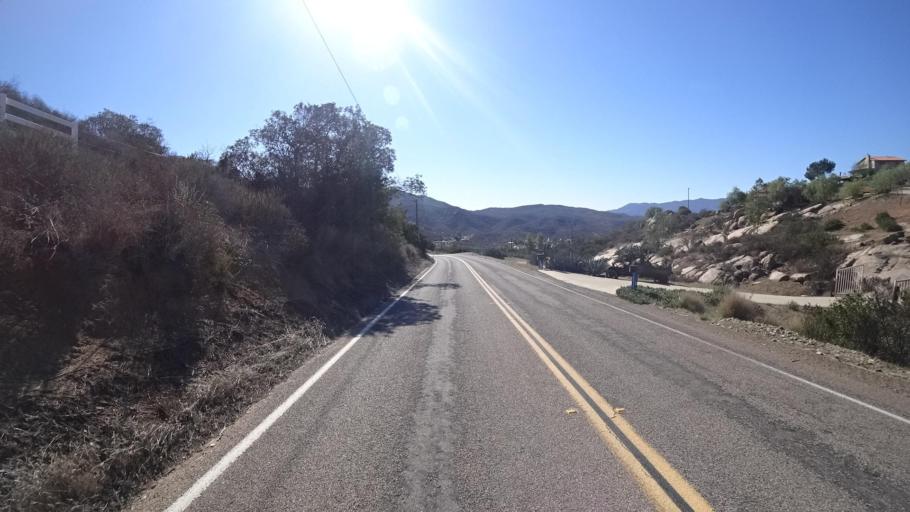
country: US
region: California
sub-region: San Diego County
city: Jamul
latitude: 32.7134
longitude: -116.7999
